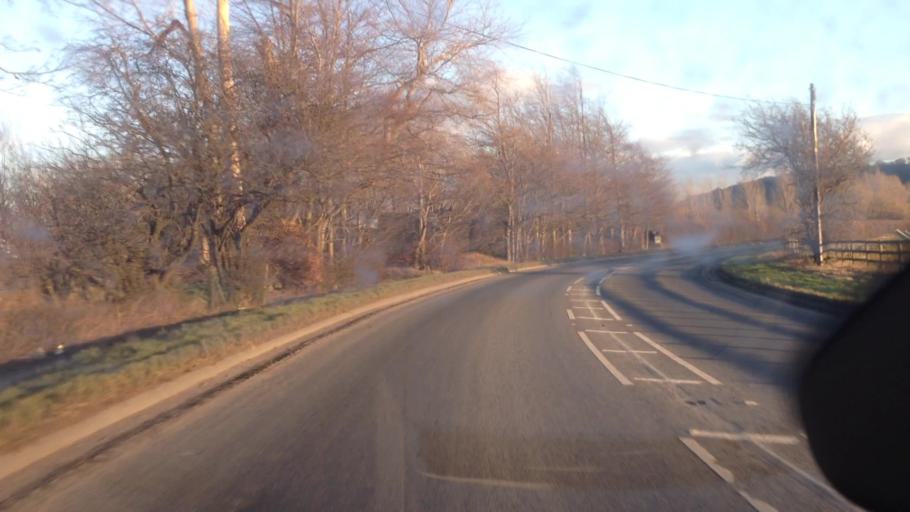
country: GB
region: England
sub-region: City and Borough of Leeds
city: Otley
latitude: 53.9097
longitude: -1.6621
